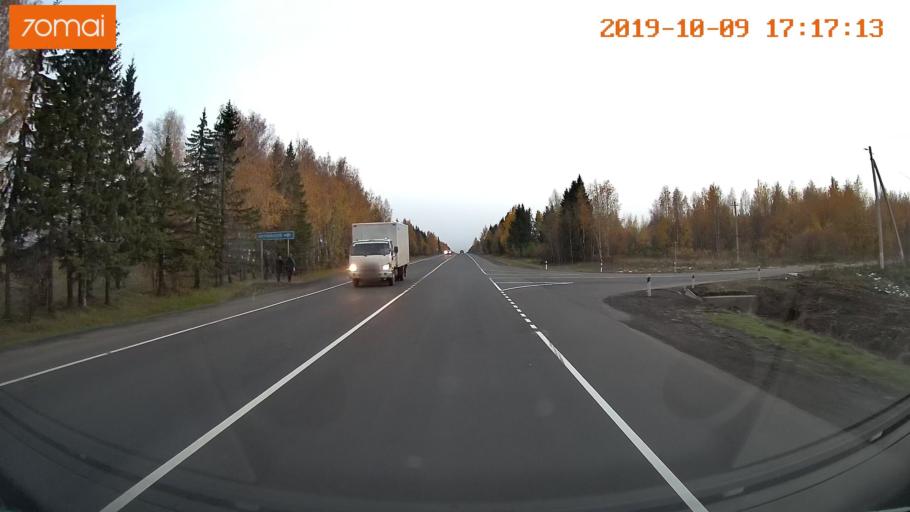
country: RU
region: Ivanovo
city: Furmanov
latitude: 57.2790
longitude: 41.1588
